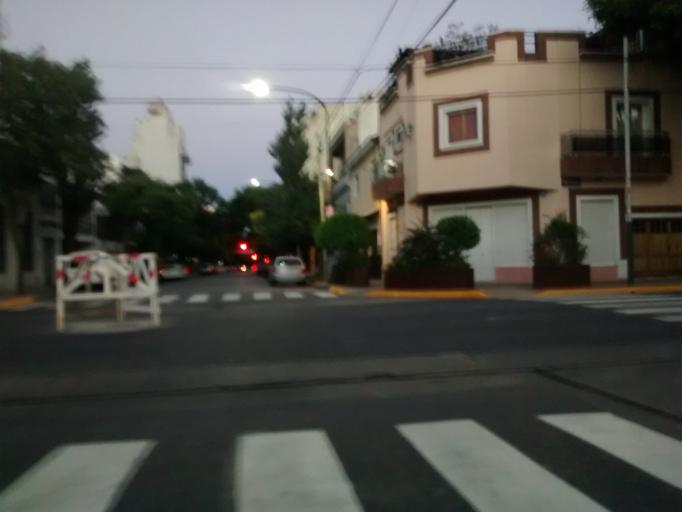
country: AR
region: Buenos Aires F.D.
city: Villa Santa Rita
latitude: -34.6123
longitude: -58.4530
